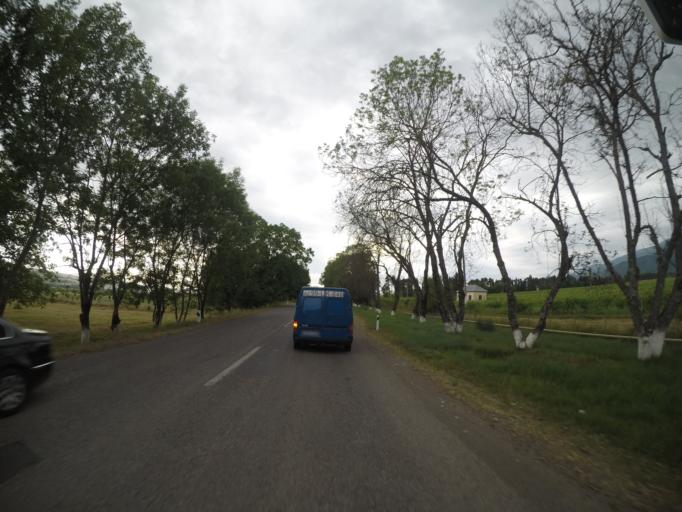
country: AZ
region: Ismayilli
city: Ismayilli
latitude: 40.7760
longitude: 48.1960
